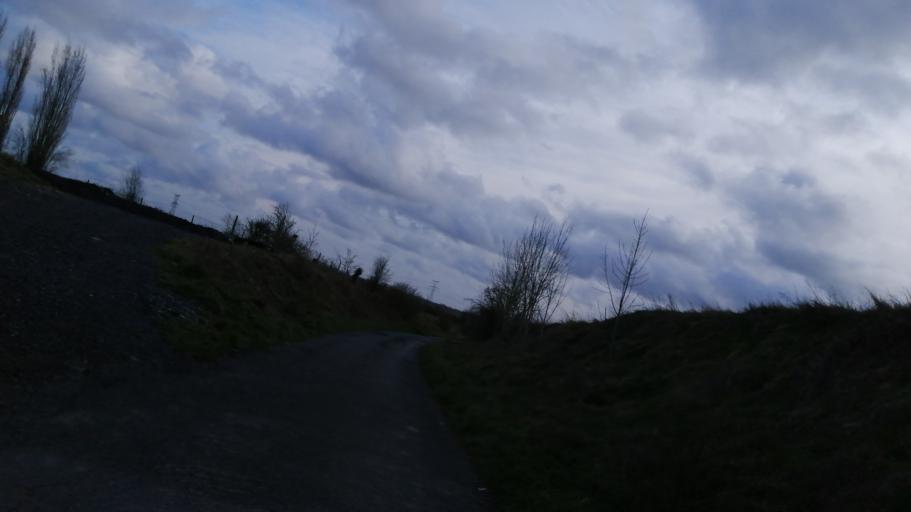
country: FR
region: Nord-Pas-de-Calais
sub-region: Departement du Pas-de-Calais
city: Beaurains
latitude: 50.2541
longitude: 2.7865
